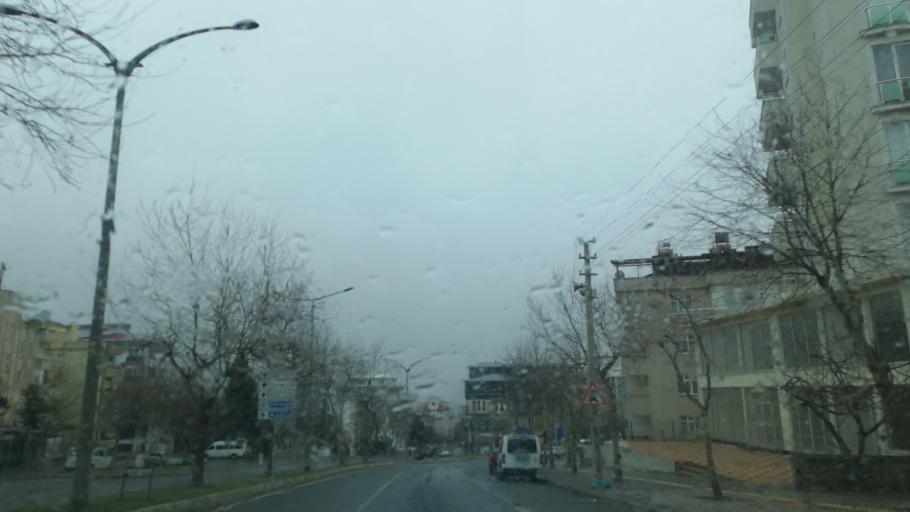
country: TR
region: Kahramanmaras
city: Kahramanmaras
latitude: 37.5907
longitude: 36.9020
